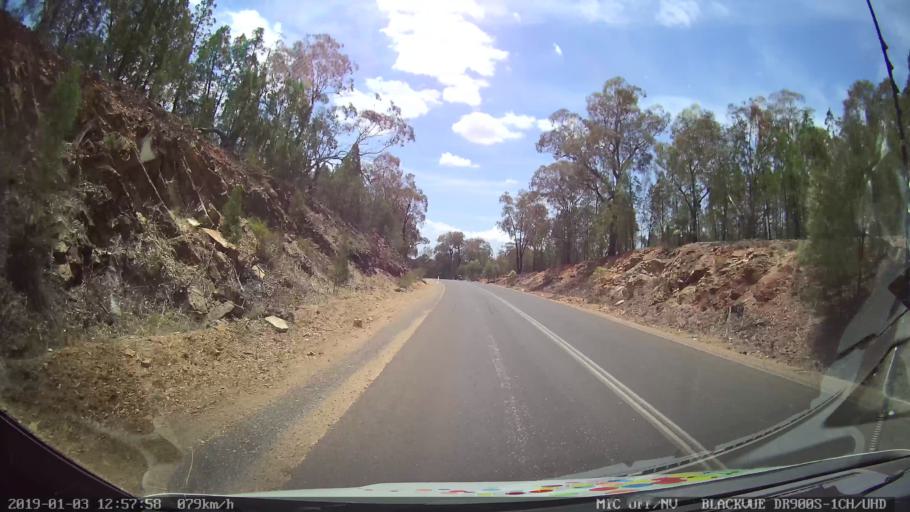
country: AU
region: New South Wales
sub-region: Cabonne
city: Canowindra
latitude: -33.6457
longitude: 148.3692
